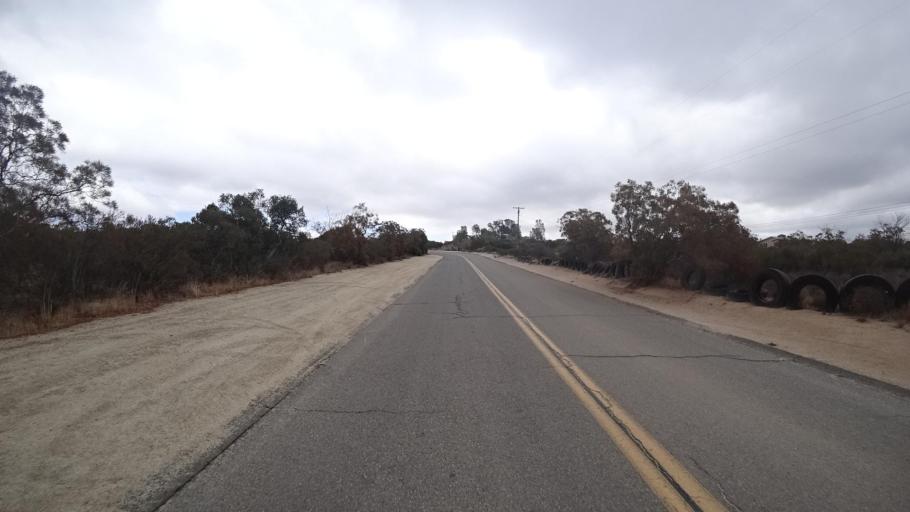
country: US
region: California
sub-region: San Diego County
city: Campo
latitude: 32.6056
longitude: -116.3353
